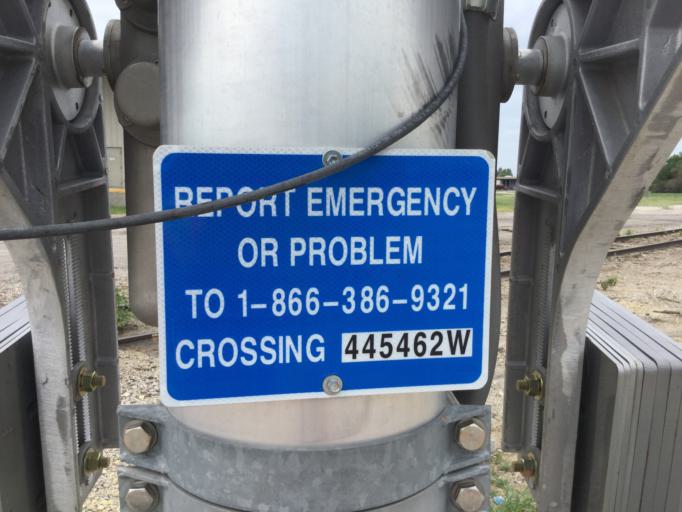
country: US
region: Kansas
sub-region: Harvey County
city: Hesston
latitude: 38.1403
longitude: -97.4317
